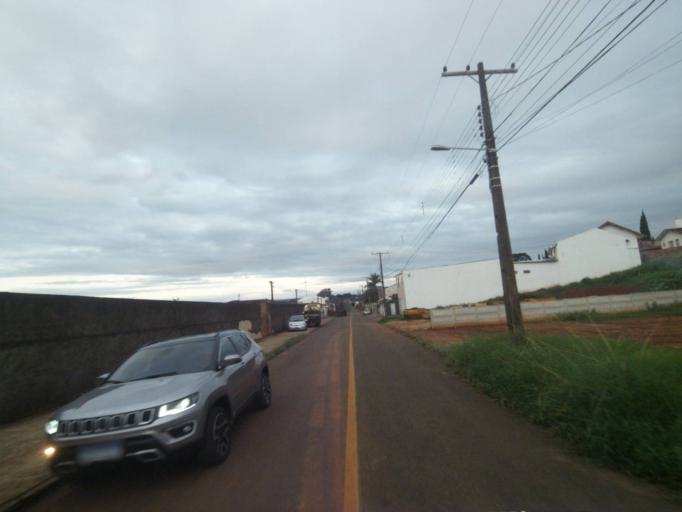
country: BR
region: Parana
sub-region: Telemaco Borba
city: Telemaco Borba
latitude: -24.3323
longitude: -50.6326
